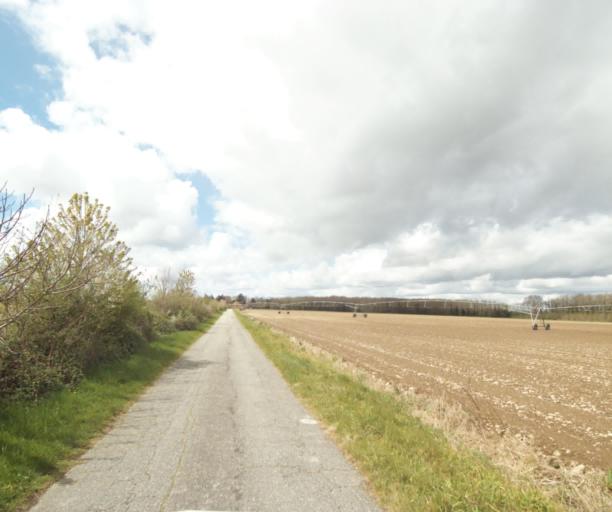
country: FR
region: Midi-Pyrenees
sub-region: Departement de la Haute-Garonne
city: Calmont
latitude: 43.2543
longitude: 1.6323
